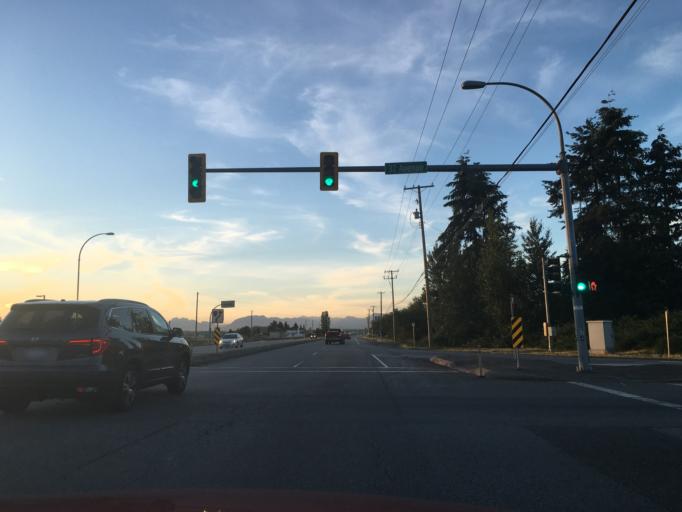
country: US
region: Washington
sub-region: Whatcom County
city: Blaine
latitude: 49.0600
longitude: -122.7352
